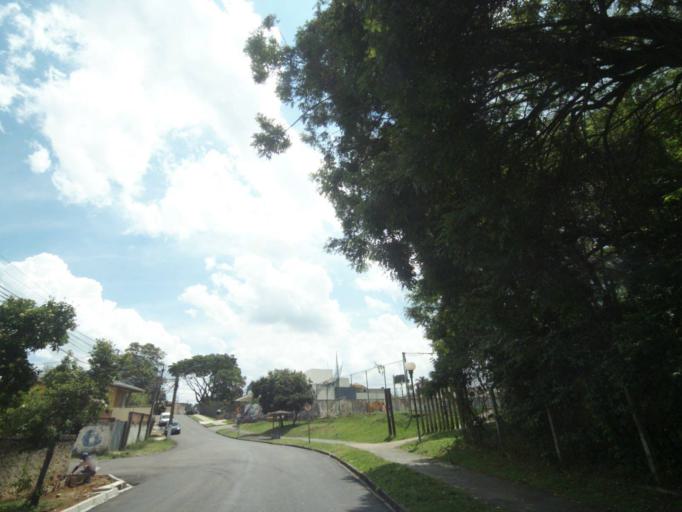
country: BR
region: Parana
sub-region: Curitiba
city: Curitiba
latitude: -25.4644
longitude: -49.3414
